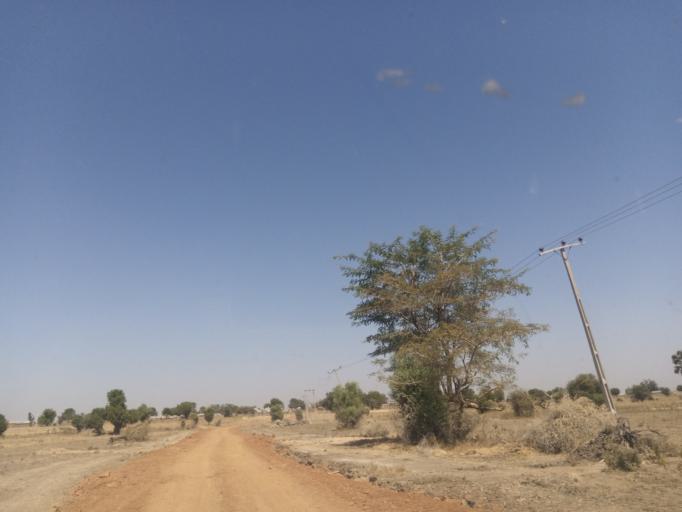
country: NG
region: Adamawa
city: Yola
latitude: 9.3067
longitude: 12.8897
